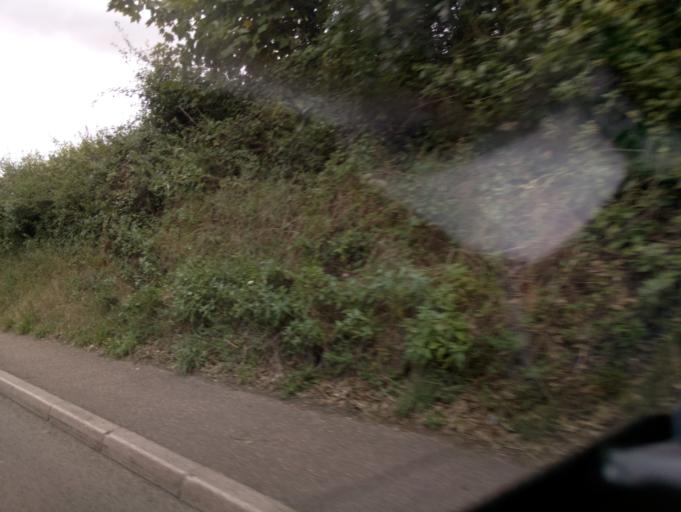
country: GB
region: England
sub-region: Devon
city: Dawlish
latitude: 50.5772
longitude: -3.4682
